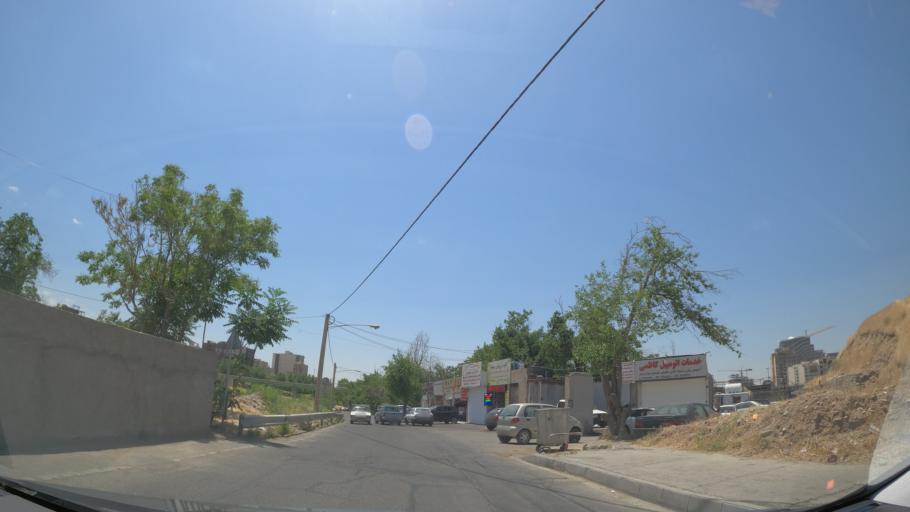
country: IR
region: Tehran
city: Tajrish
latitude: 35.7806
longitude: 51.3896
